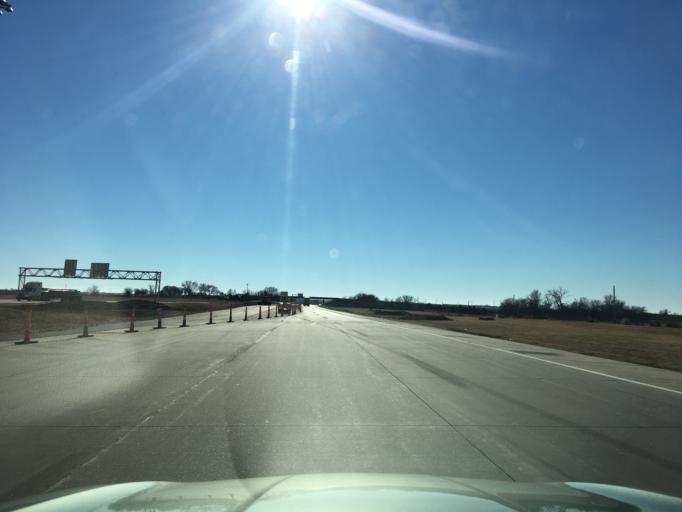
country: US
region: Kansas
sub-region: Sumner County
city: Wellington
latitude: 37.2370
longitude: -97.3392
